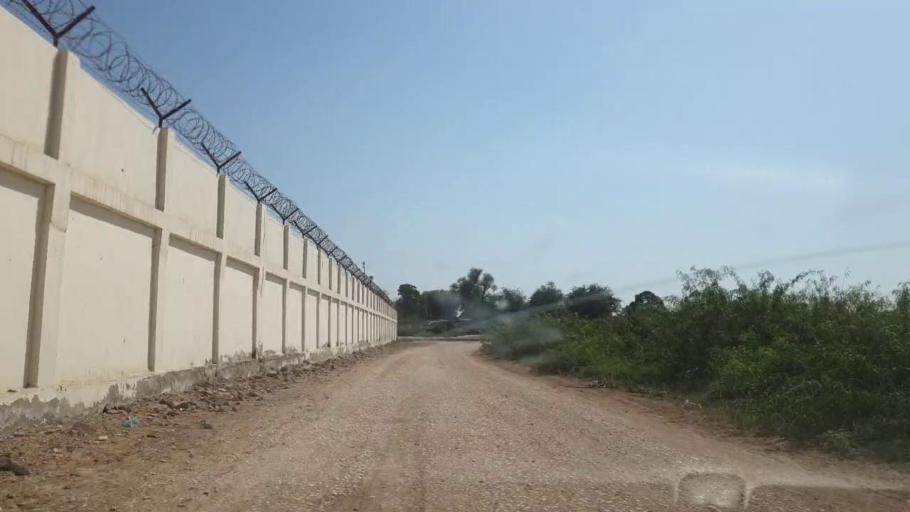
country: PK
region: Sindh
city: Tando Jam
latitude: 25.3797
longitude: 68.5800
